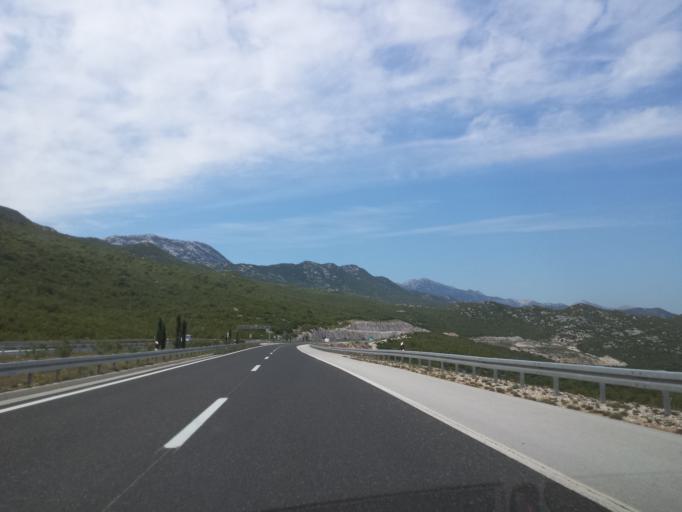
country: HR
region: Splitsko-Dalmatinska
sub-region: Grad Omis
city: Omis
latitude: 43.4793
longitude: 16.8184
